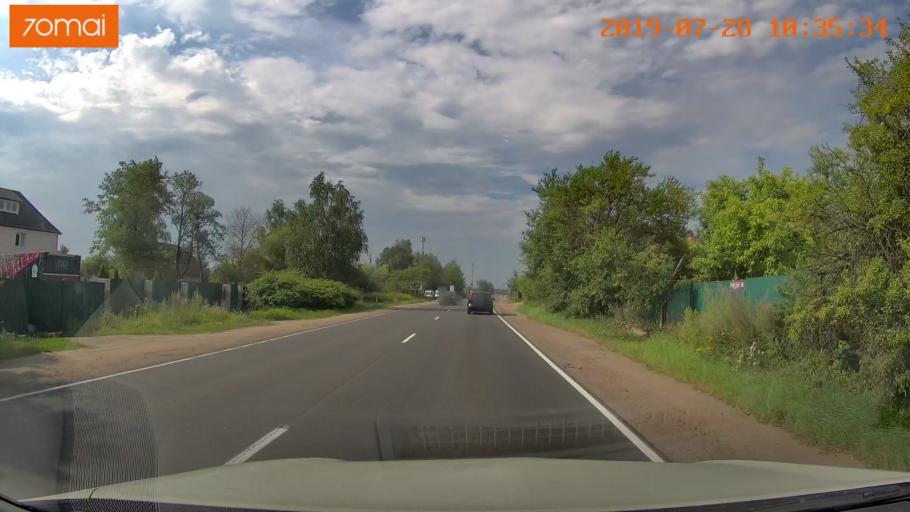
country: RU
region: Kaliningrad
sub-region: Gorod Kaliningrad
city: Kaliningrad
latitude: 54.7456
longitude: 20.4304
